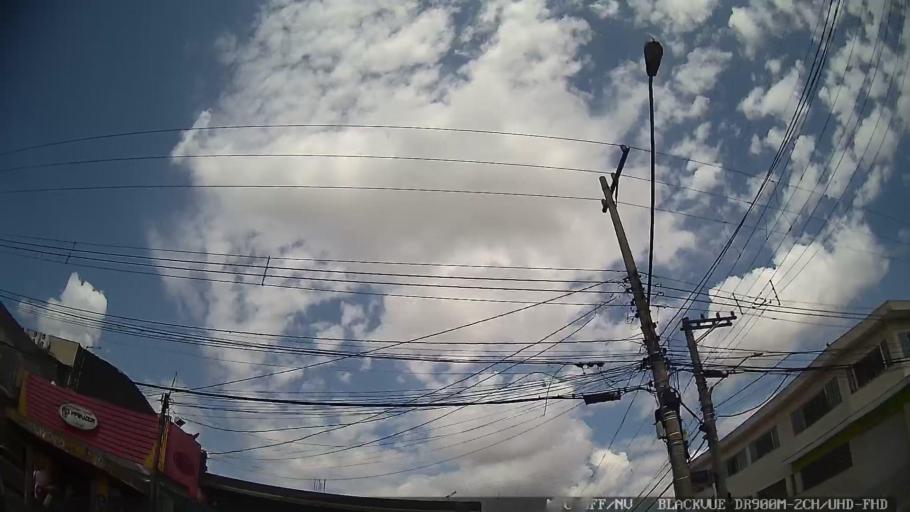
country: BR
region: Sao Paulo
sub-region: Guarulhos
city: Guarulhos
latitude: -23.5170
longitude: -46.4682
